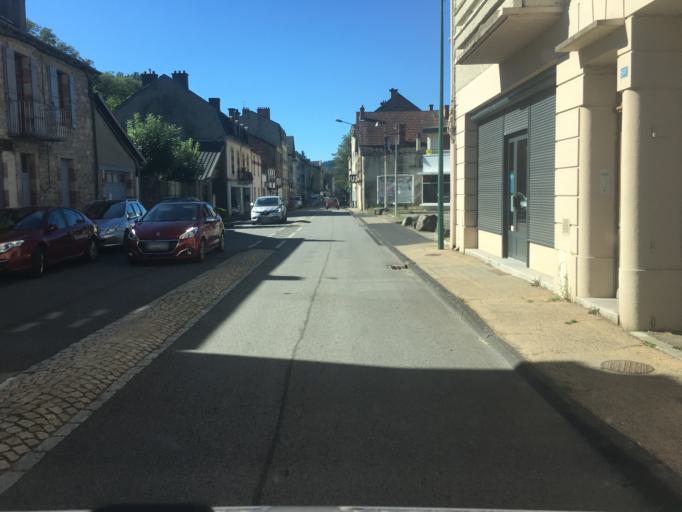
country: FR
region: Limousin
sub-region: Departement de la Correze
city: Bort-les-Orgues
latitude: 45.4051
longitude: 2.5016
